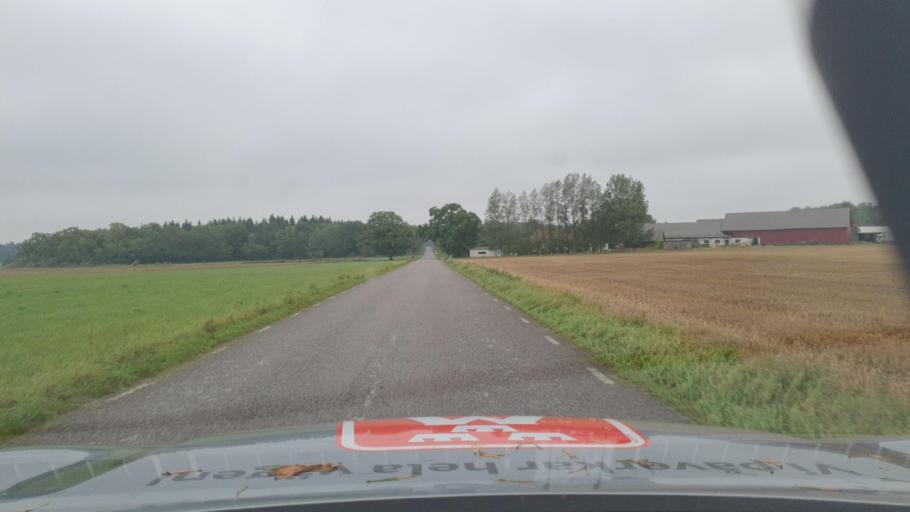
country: SE
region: Gotland
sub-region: Gotland
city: Visby
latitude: 57.7748
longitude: 18.4965
